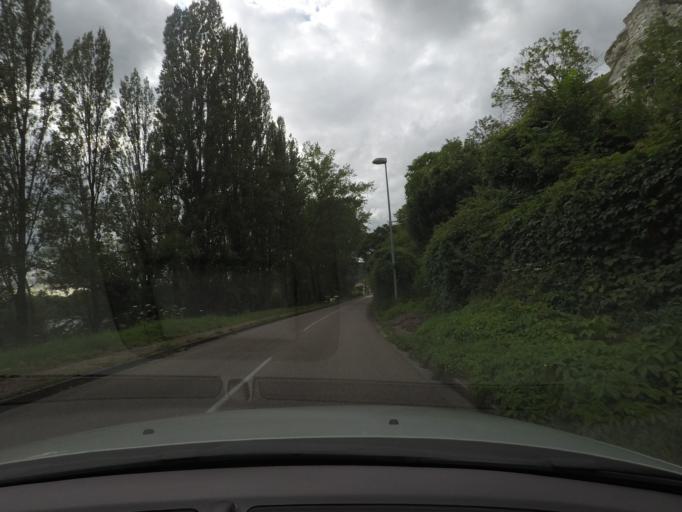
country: FR
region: Haute-Normandie
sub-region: Departement de l'Eure
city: Les Andelys
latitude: 49.2475
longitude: 1.3922
